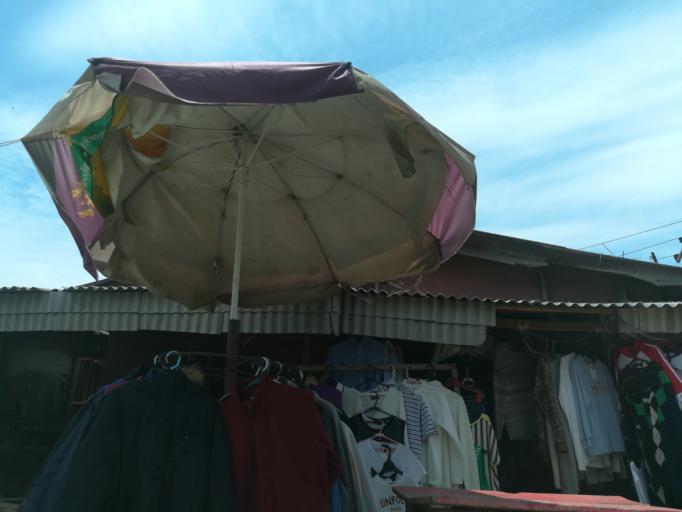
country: NG
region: Lagos
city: Ebute Ikorodu
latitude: 6.6024
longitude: 3.4876
